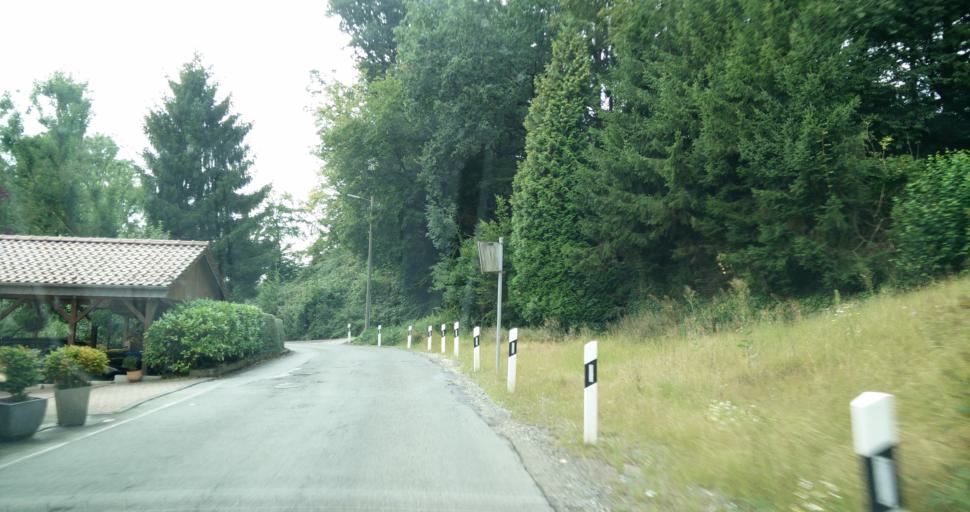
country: DE
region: North Rhine-Westphalia
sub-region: Regierungsbezirk Dusseldorf
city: Ratingen
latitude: 51.2825
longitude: 6.8833
